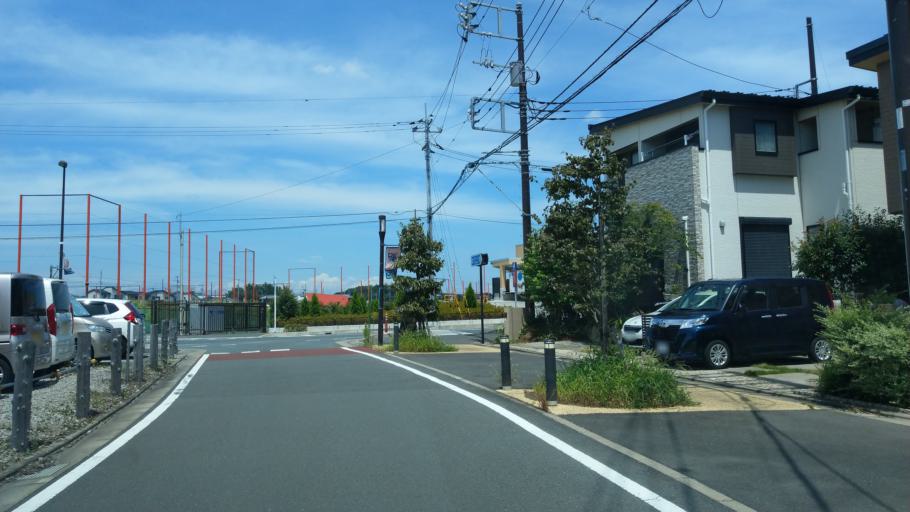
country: JP
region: Saitama
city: Ageoshimo
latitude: 35.9304
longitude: 139.5781
